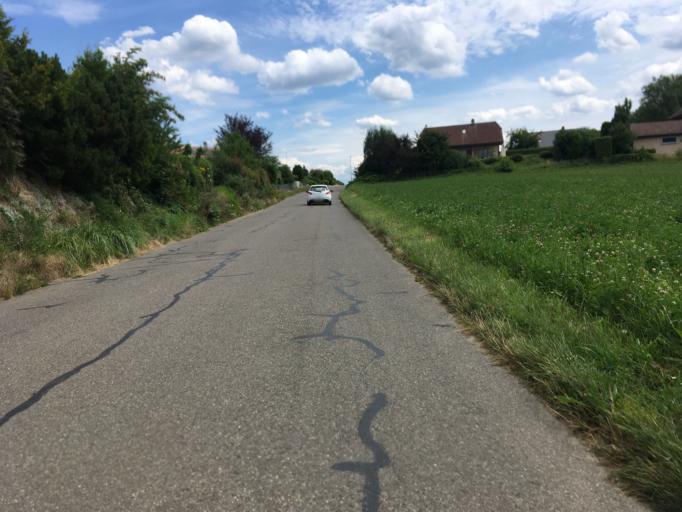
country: CH
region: Fribourg
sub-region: Broye District
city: Estavayer-le-Lac
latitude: 46.8689
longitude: 6.8817
